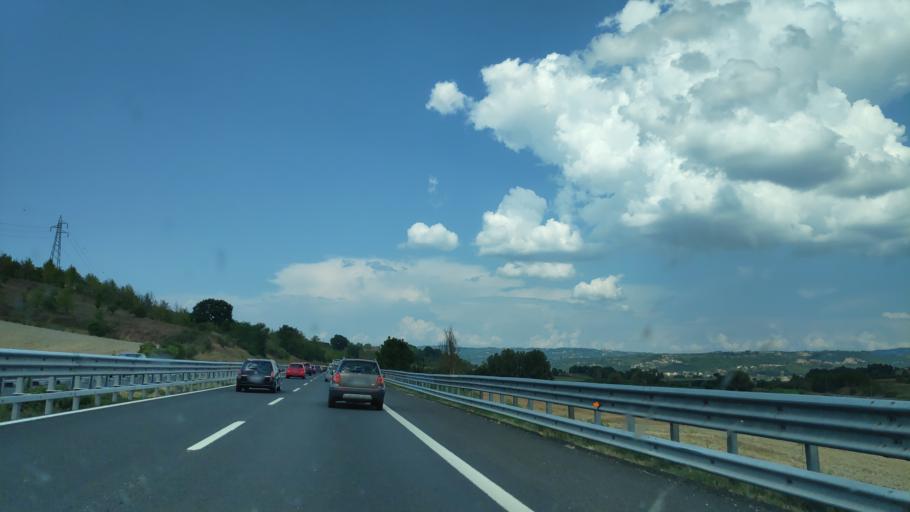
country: IT
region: Umbria
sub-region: Provincia di Terni
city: Fabro Scalo
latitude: 42.8485
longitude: 12.0384
